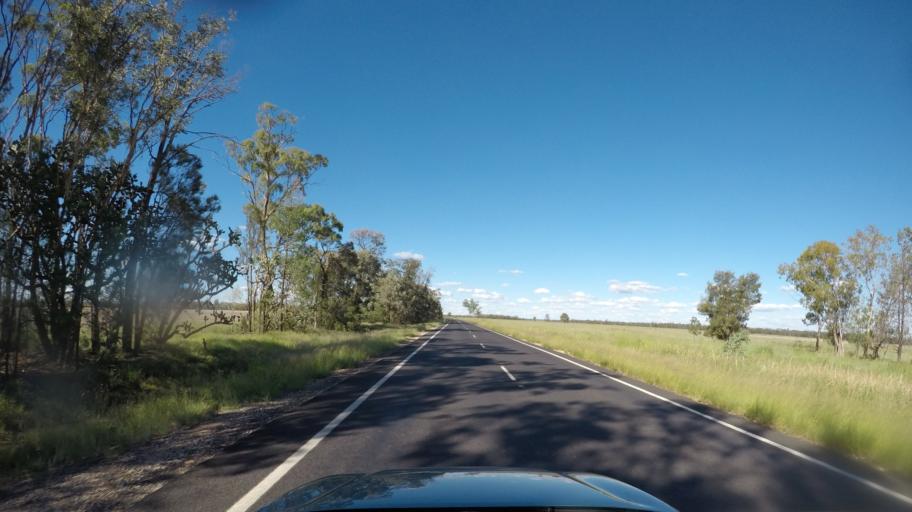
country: AU
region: Queensland
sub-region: Goondiwindi
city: Goondiwindi
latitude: -28.1398
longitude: 150.6923
